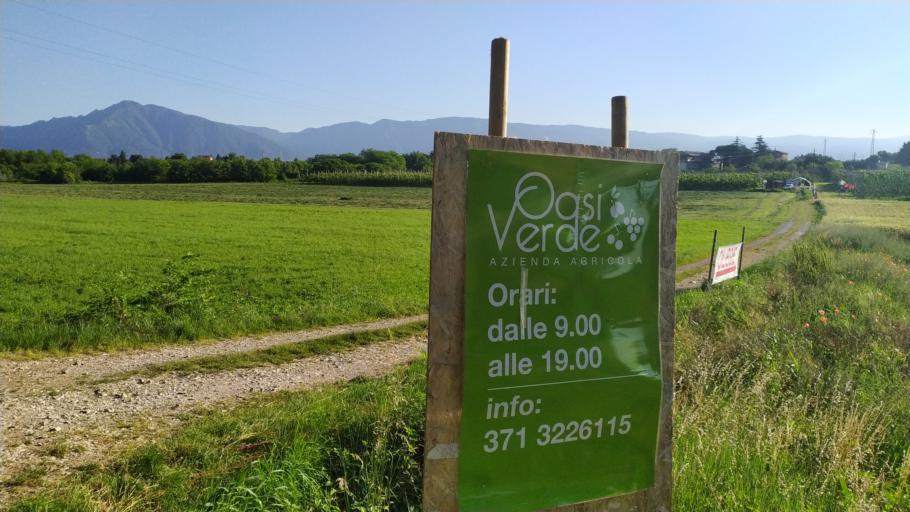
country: IT
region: Veneto
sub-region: Provincia di Vicenza
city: Malo
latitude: 45.6485
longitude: 11.4162
